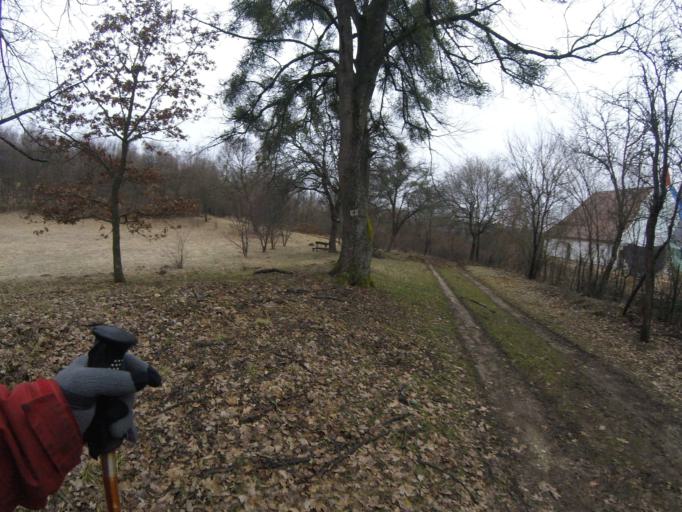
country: HU
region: Borsod-Abauj-Zemplen
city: Rudabanya
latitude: 48.4602
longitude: 20.6173
